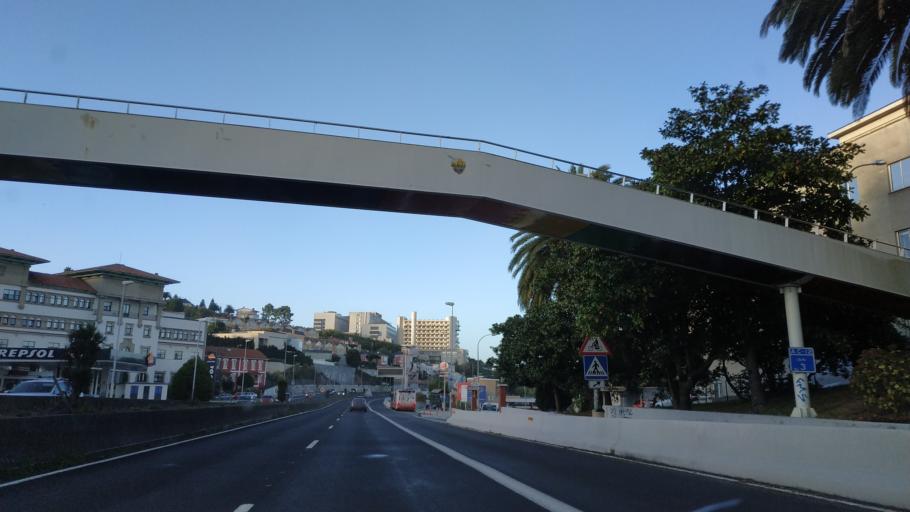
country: ES
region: Galicia
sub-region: Provincia da Coruna
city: A Coruna
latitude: 43.3385
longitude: -8.3889
